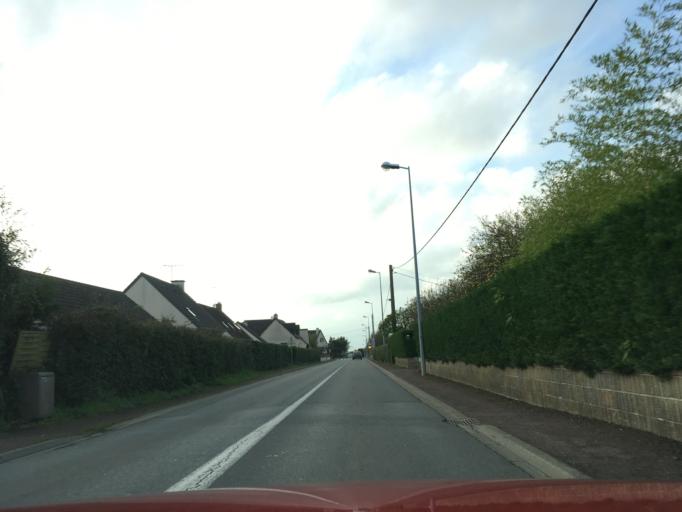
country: FR
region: Lower Normandy
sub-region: Departement de la Manche
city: Saint-Pair-sur-Mer
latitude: 48.8149
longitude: -1.5562
